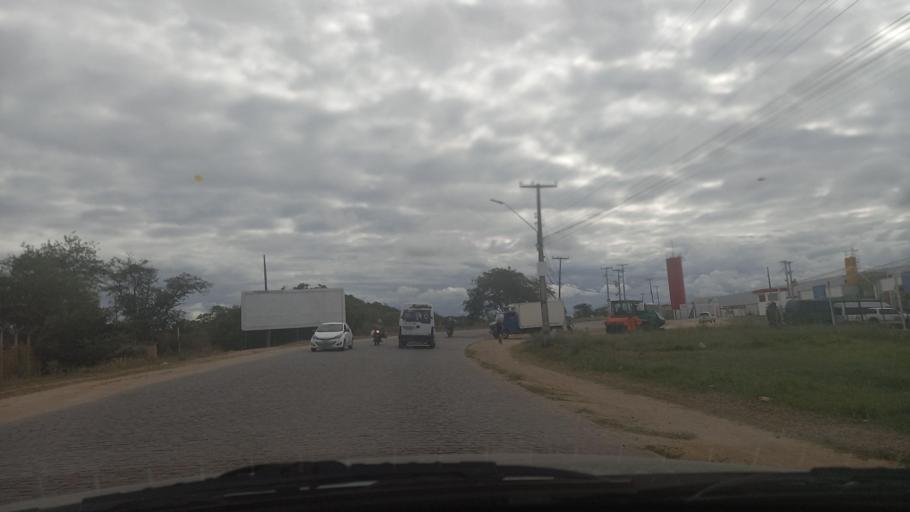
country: BR
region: Pernambuco
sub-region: Caruaru
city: Caruaru
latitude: -8.2899
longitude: -36.0187
